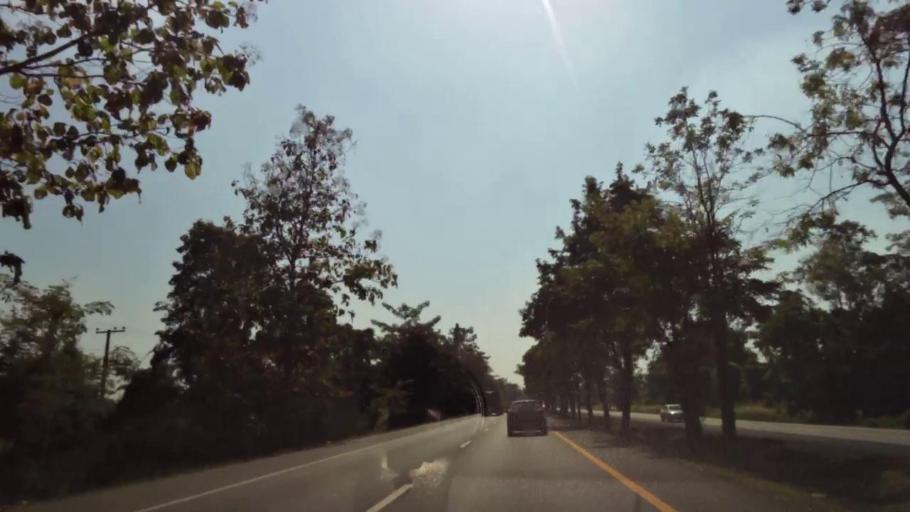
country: TH
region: Phichit
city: Bueng Na Rang
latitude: 16.0530
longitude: 100.1214
